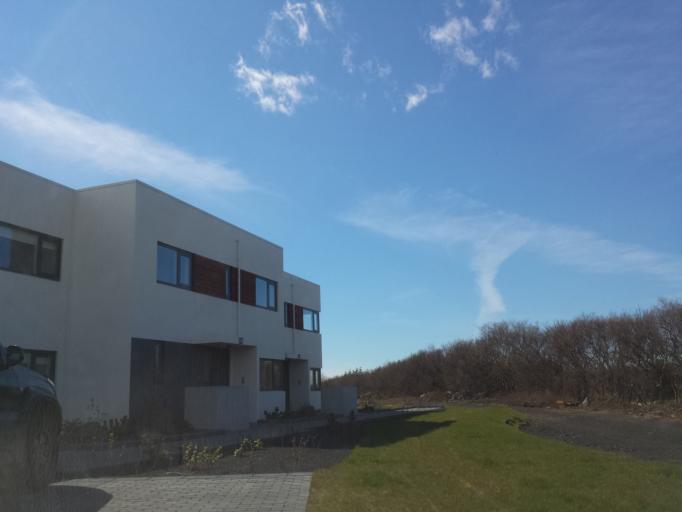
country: IS
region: Capital Region
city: Reykjavik
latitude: 64.1168
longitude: -21.8902
